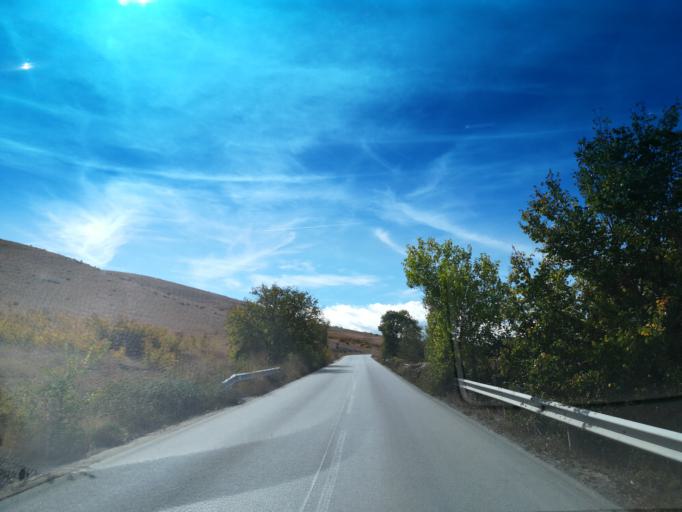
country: BG
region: Plovdiv
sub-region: Obshtina Krichim
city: Krichim
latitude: 42.1000
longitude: 24.4670
